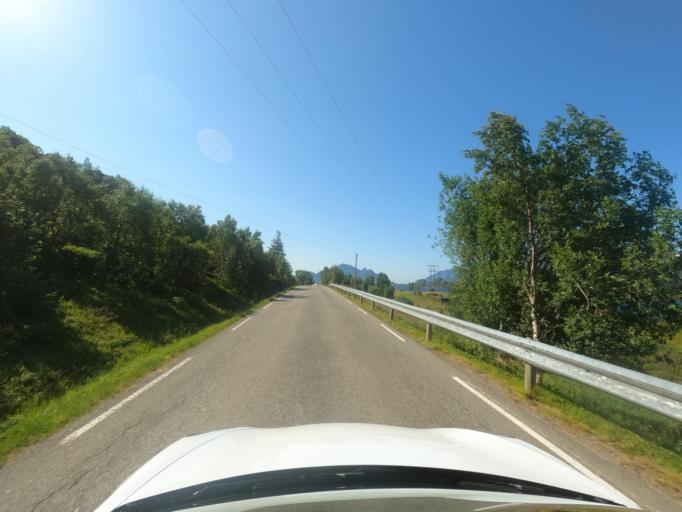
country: NO
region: Nordland
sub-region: Hadsel
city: Stokmarknes
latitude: 68.3597
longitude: 15.0653
